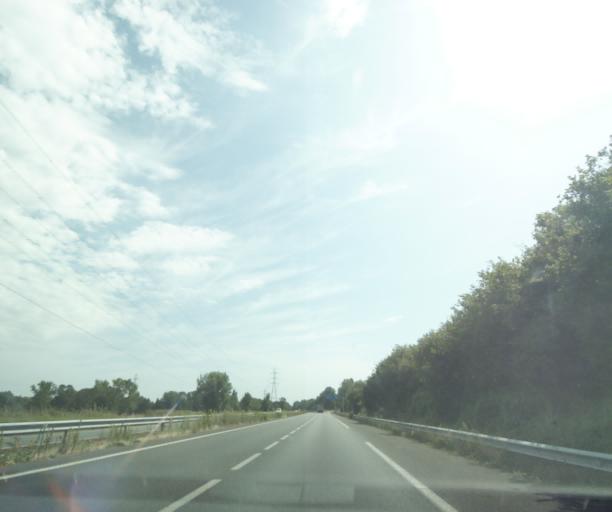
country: FR
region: Aquitaine
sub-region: Departement de la Gironde
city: Saint-Christoly-de-Blaye
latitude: 45.1125
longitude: -0.4846
